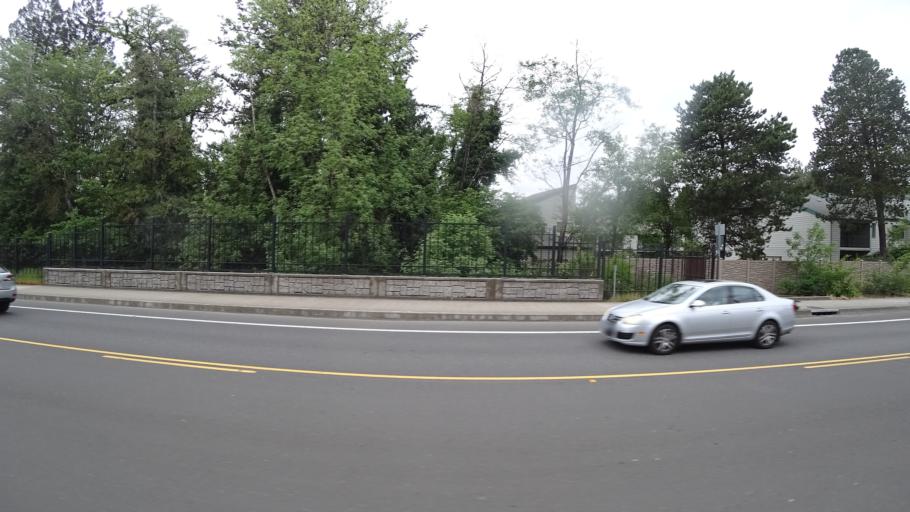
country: US
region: Oregon
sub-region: Washington County
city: Raleigh Hills
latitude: 45.4706
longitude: -122.7751
